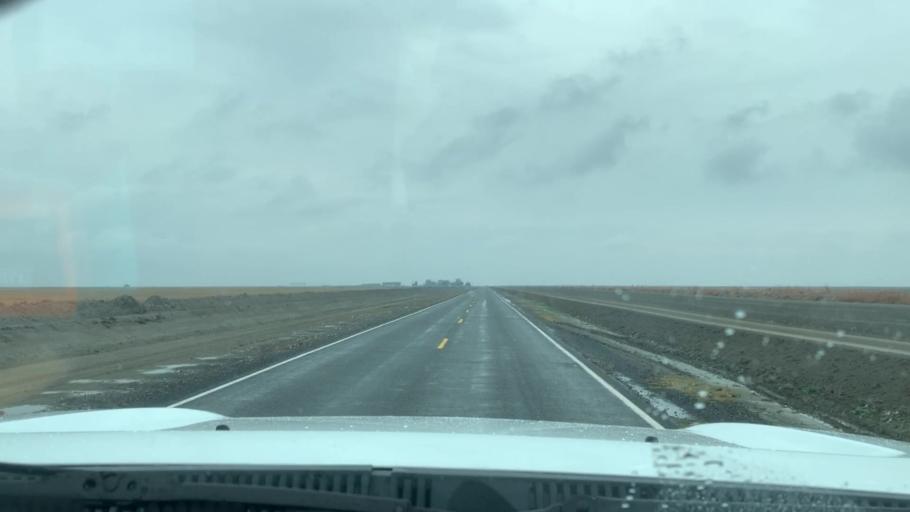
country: US
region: California
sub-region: Tulare County
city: Alpaugh
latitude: 35.9342
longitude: -119.6277
